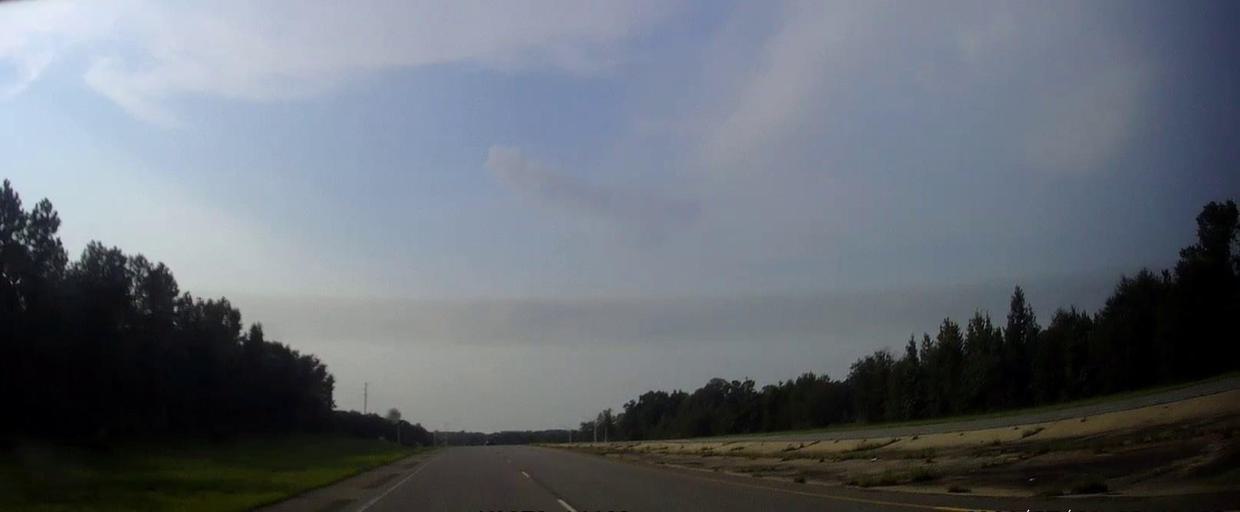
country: US
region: Georgia
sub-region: Laurens County
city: Dublin
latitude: 32.5327
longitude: -82.9686
